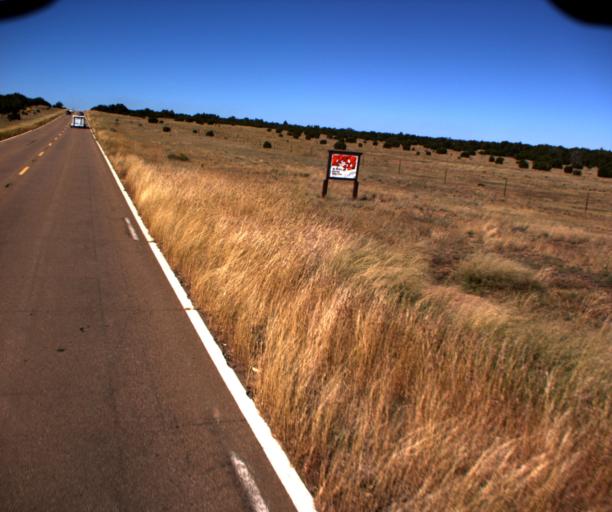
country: US
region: Arizona
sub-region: Navajo County
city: Heber-Overgaard
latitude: 34.4606
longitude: -110.4930
